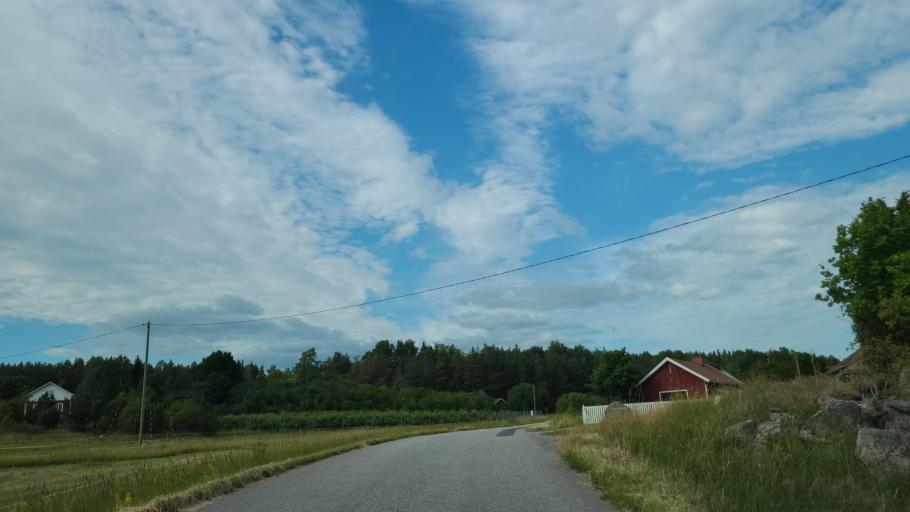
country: FI
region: Varsinais-Suomi
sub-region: Turku
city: Rymaettylae
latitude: 60.2978
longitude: 21.9371
